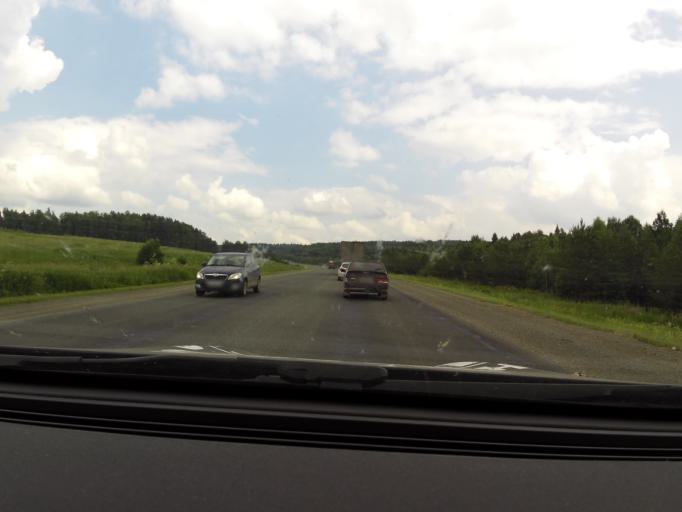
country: RU
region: Sverdlovsk
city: Ufimskiy
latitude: 56.7821
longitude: 58.2812
